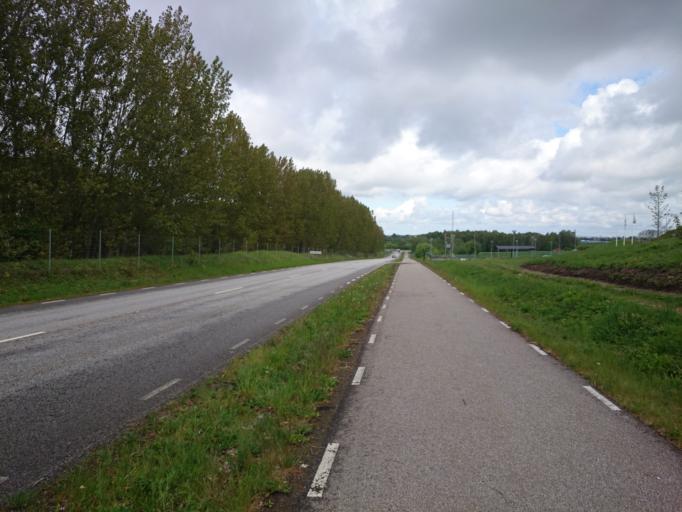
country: SE
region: Skane
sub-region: Malmo
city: Oxie
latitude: 55.5703
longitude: 13.0855
